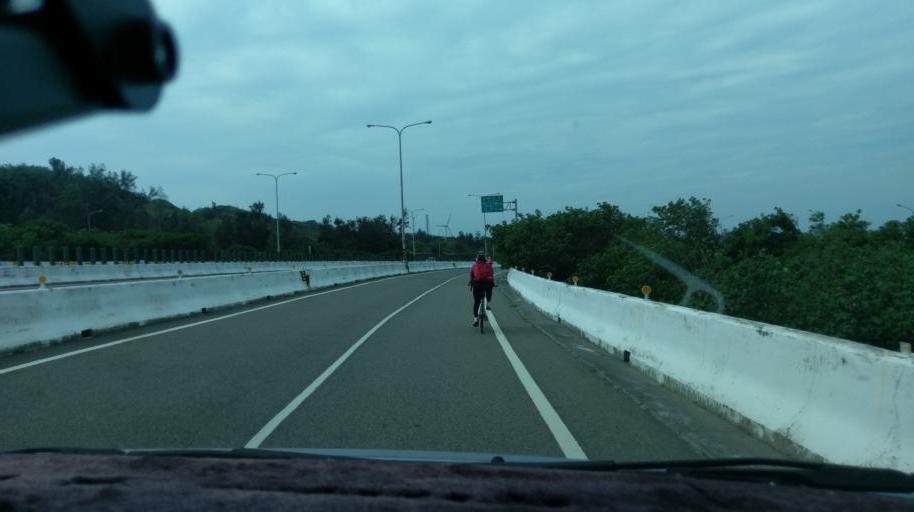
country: TW
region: Taiwan
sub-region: Miaoli
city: Miaoli
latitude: 24.6112
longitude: 120.7591
